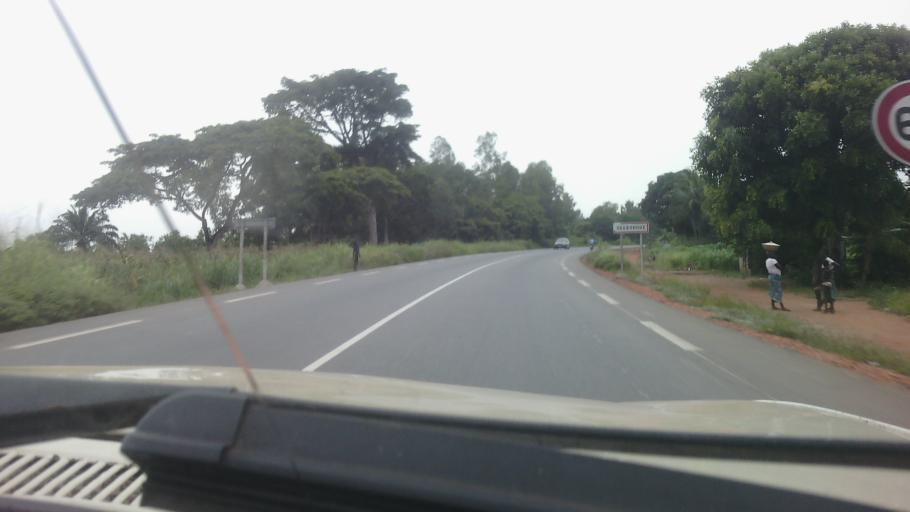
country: BJ
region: Mono
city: Come
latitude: 6.3971
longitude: 1.9561
